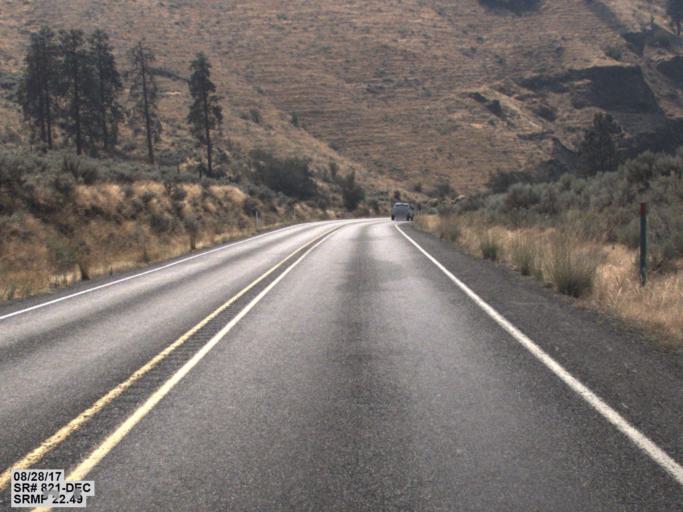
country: US
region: Washington
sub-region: Kittitas County
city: Ellensburg
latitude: 46.8995
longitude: -120.4940
